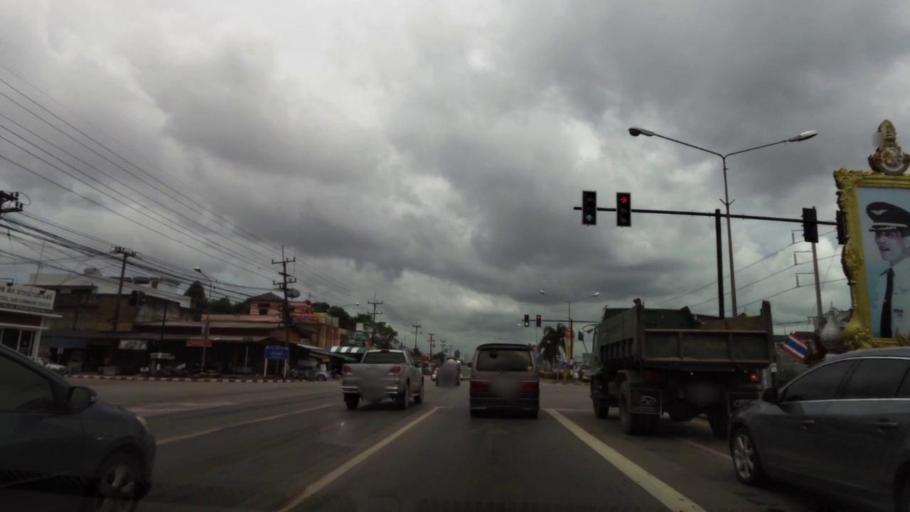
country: TH
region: Rayong
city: Klaeng
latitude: 12.7805
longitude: 101.7330
